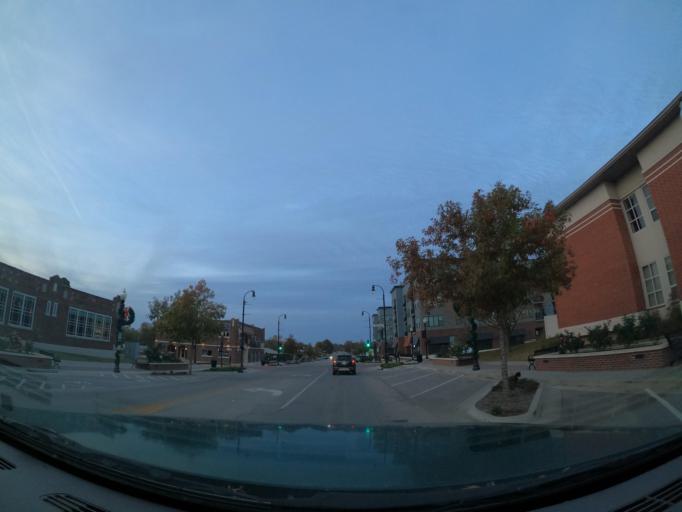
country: US
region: Oklahoma
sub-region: Tulsa County
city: Broken Arrow
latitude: 36.0542
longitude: -95.7908
